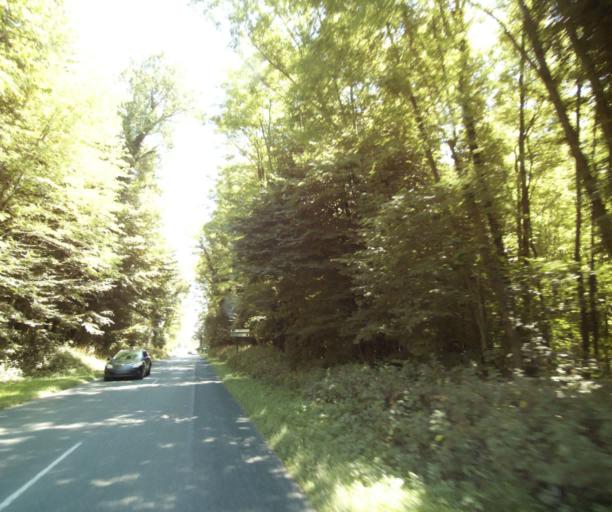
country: FR
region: Ile-de-France
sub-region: Departement de Seine-et-Marne
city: Noisy-sur-Ecole
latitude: 48.3718
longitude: 2.5084
